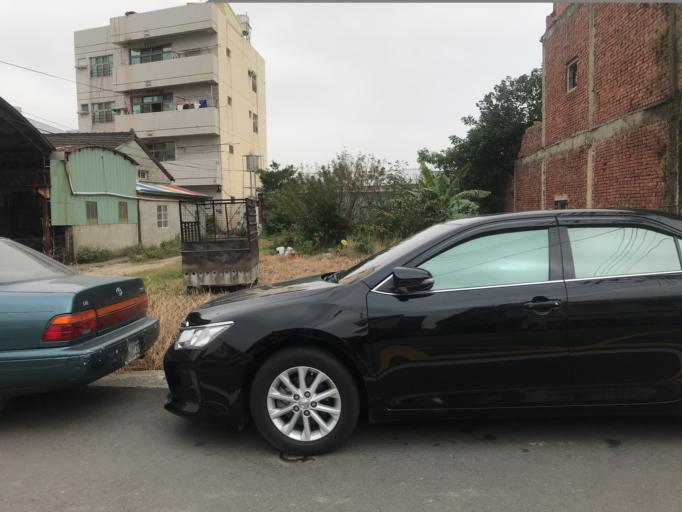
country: TW
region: Taiwan
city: Fengyuan
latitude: 24.3553
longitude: 120.6097
